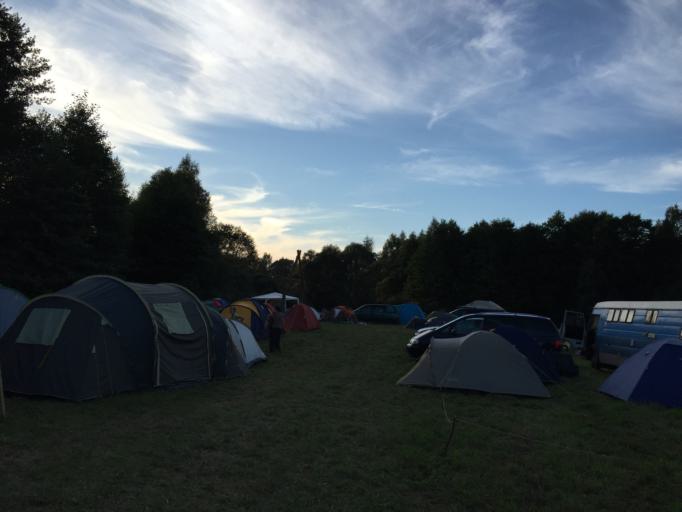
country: LT
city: Zarasai
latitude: 55.7891
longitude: 25.9619
